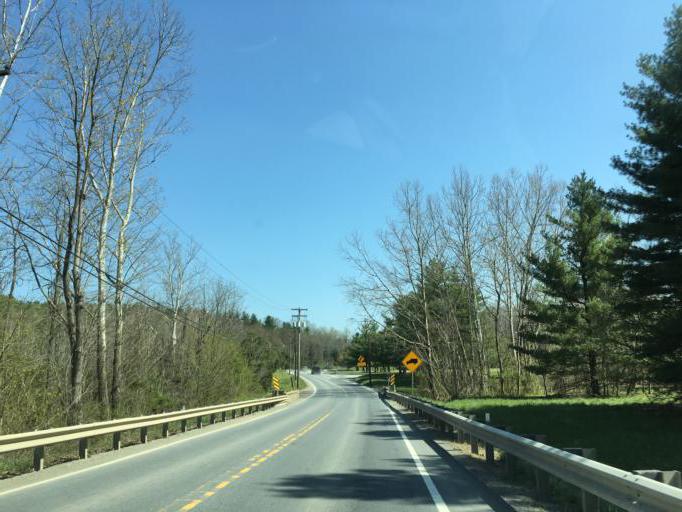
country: US
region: Maryland
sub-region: Frederick County
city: Woodsboro
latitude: 39.5275
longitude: -77.3004
